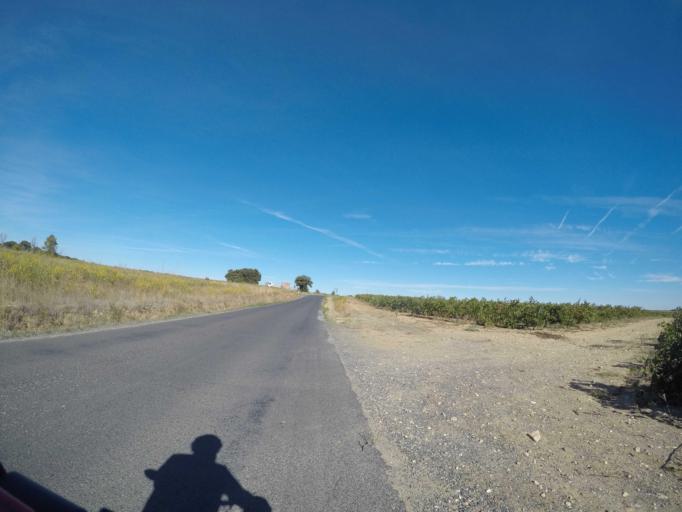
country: FR
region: Languedoc-Roussillon
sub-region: Departement des Pyrenees-Orientales
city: Ponteilla
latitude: 42.6339
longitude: 2.8088
